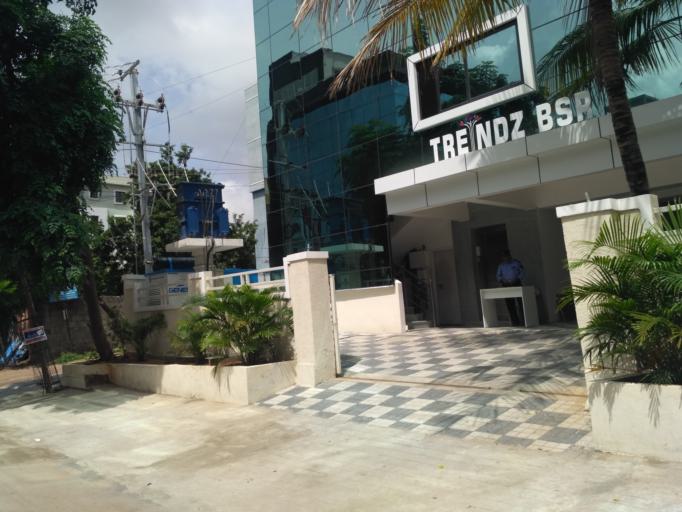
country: IN
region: Telangana
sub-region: Rangareddi
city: Kukatpalli
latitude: 17.4391
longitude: 78.3618
